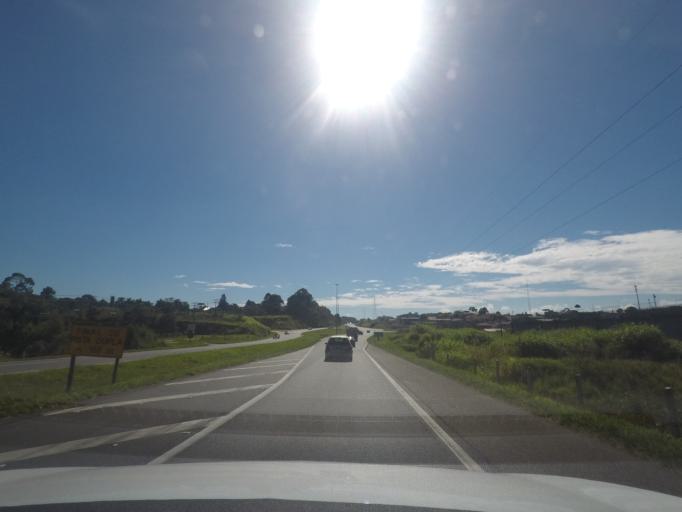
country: BR
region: Parana
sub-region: Curitiba
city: Curitiba
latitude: -25.4223
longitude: -49.3660
